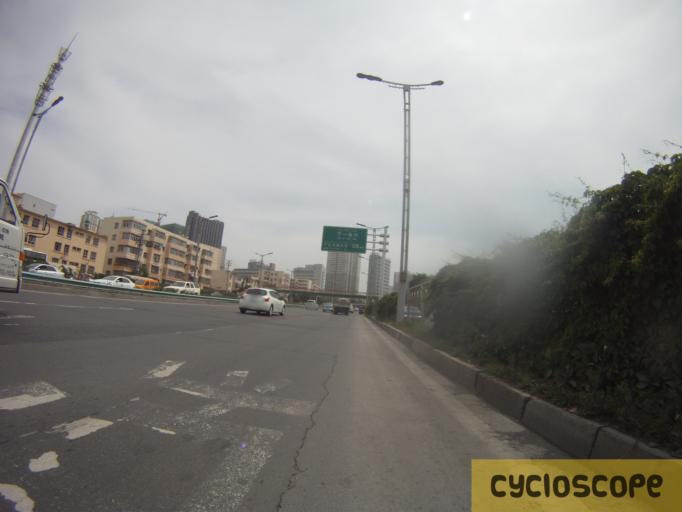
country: CN
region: Xinjiang Uygur Zizhiqu
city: UEruemqi
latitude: 43.7854
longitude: 87.6056
